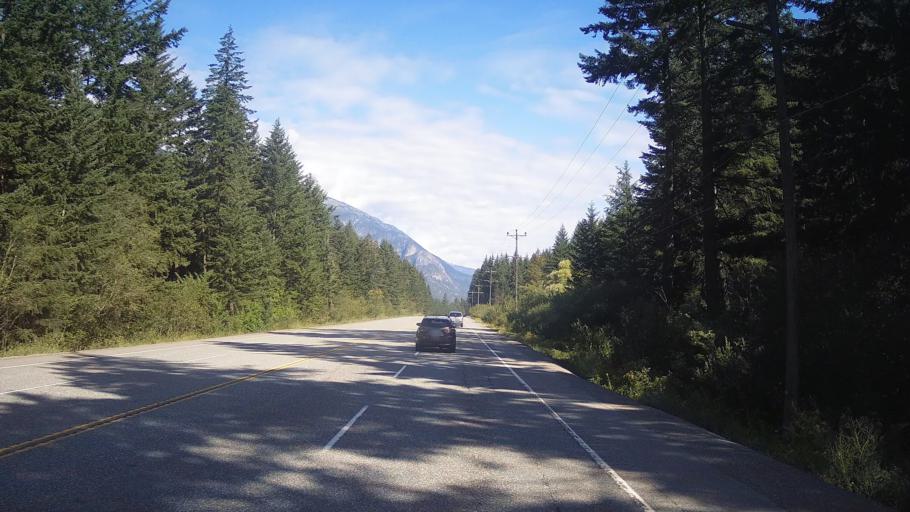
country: CA
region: British Columbia
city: Hope
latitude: 50.0424
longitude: -121.5367
